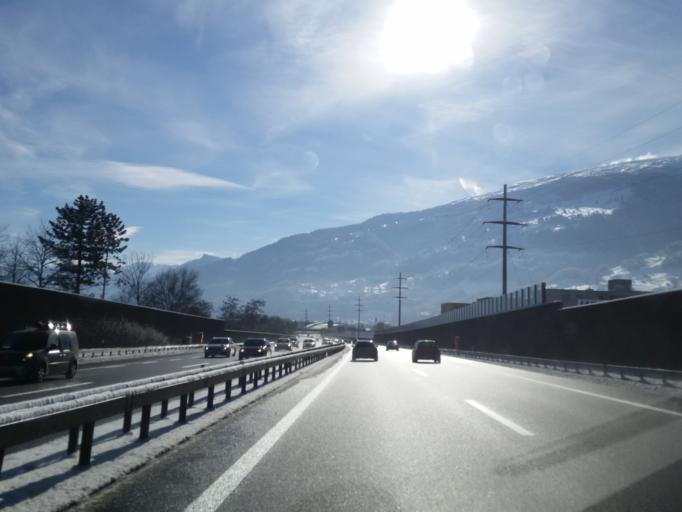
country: CH
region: Saint Gallen
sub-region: Wahlkreis Sarganserland
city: Sargans
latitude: 47.0481
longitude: 9.4311
